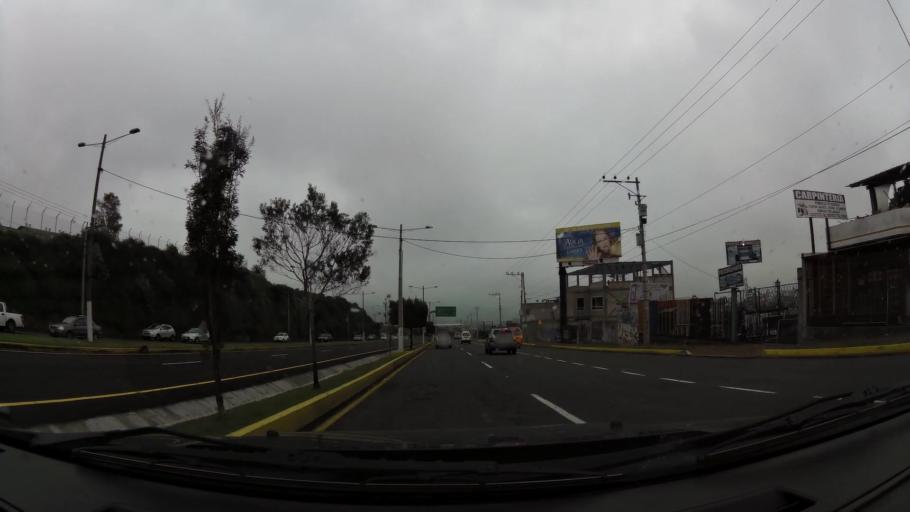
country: EC
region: Pichincha
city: Sangolqui
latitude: -0.2795
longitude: -78.4767
